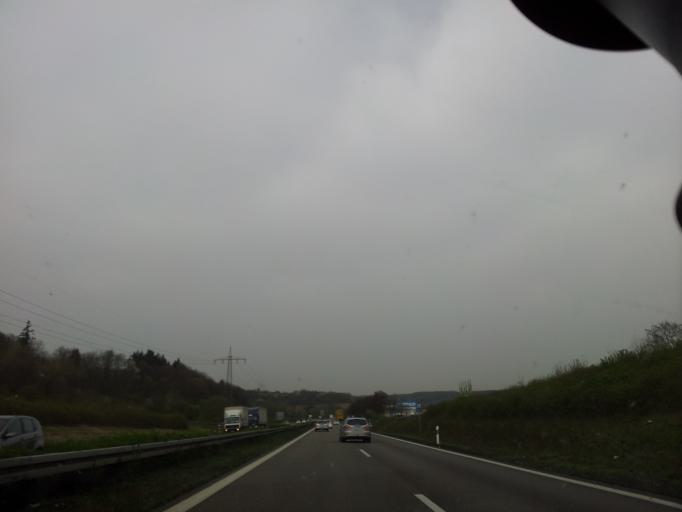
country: DE
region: Baden-Wuerttemberg
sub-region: Regierungsbezirk Stuttgart
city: Reichenbach an der Fils
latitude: 48.7029
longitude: 9.4436
